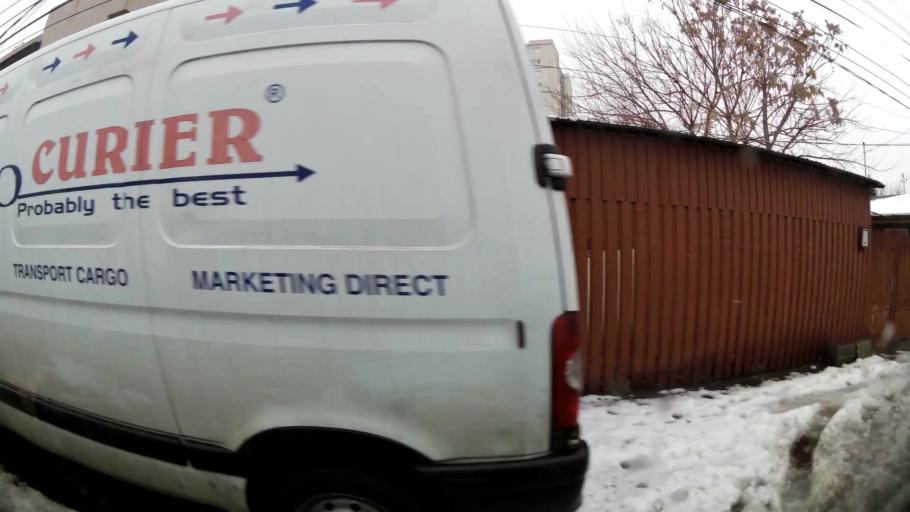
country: RO
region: Ilfov
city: Dobroesti
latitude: 44.4195
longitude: 26.1827
